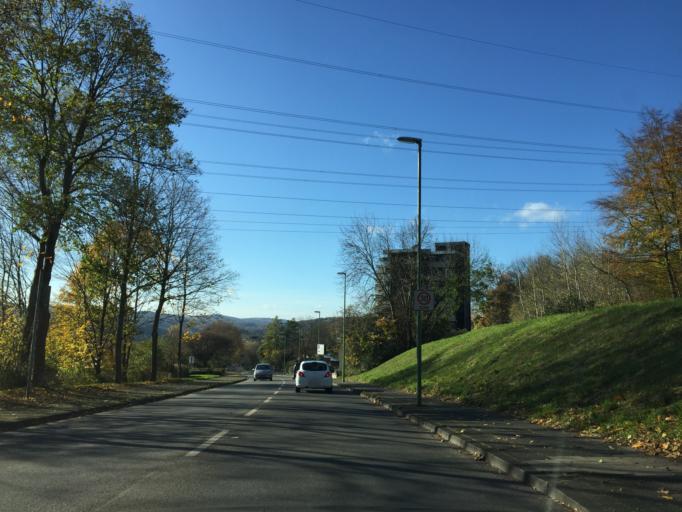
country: DE
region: North Rhine-Westphalia
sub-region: Regierungsbezirk Arnsberg
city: Nachrodt-Wiblingwerde
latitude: 51.3679
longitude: 7.5772
